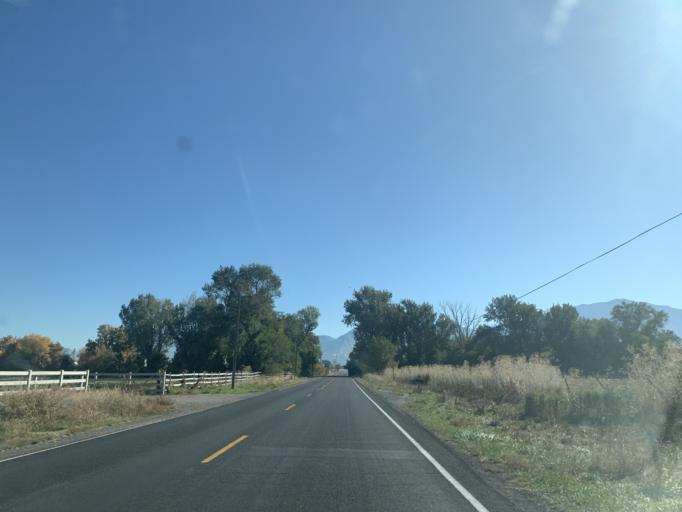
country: US
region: Utah
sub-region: Utah County
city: West Mountain
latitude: 40.0411
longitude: -111.7731
